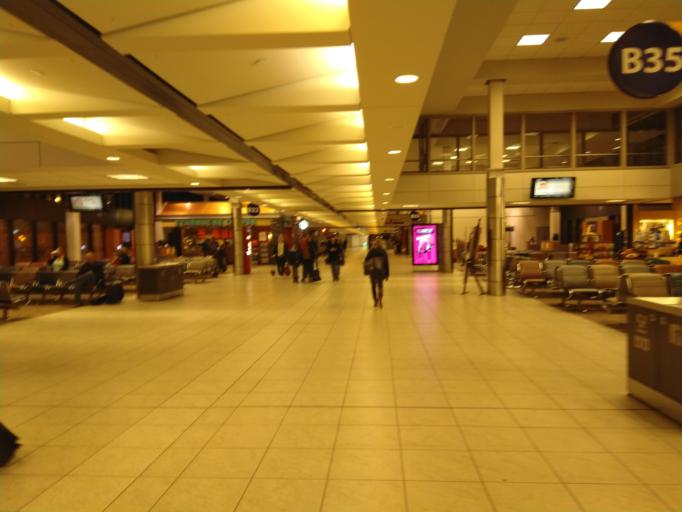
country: CA
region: Alberta
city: Calgary
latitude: 51.1303
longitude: -114.0113
